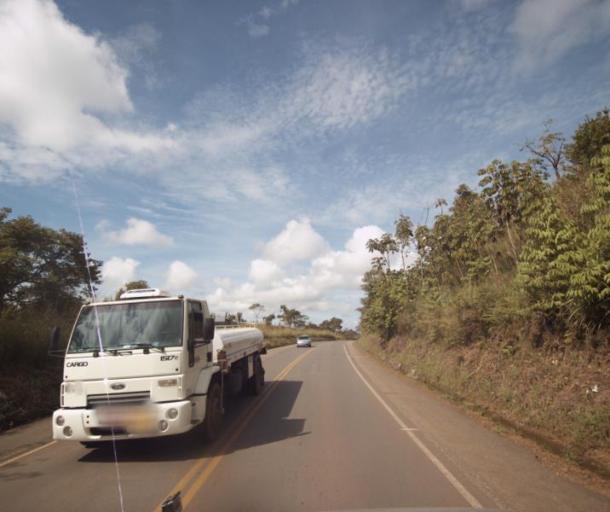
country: BR
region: Goias
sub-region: Pirenopolis
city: Pirenopolis
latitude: -15.9053
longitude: -48.8007
